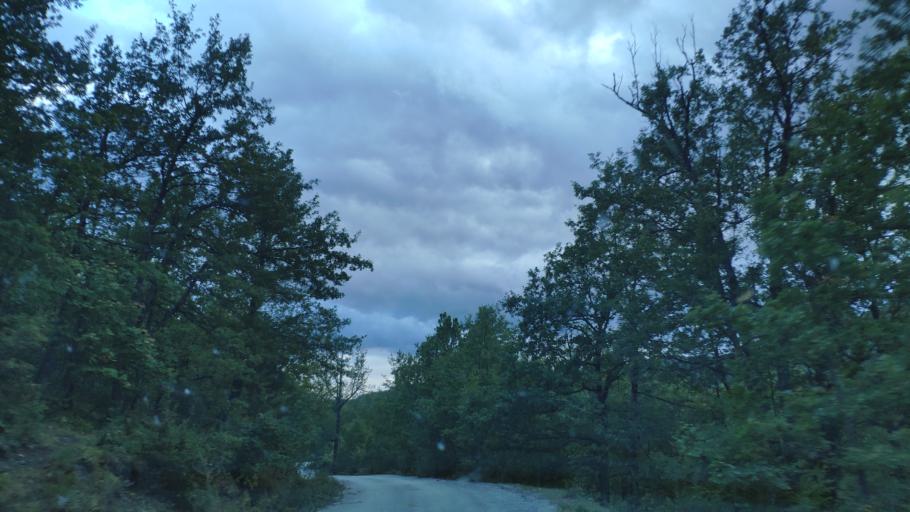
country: AL
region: Korce
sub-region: Rrethi i Kolonjes
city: Erseke
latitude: 40.2615
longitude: 20.8587
